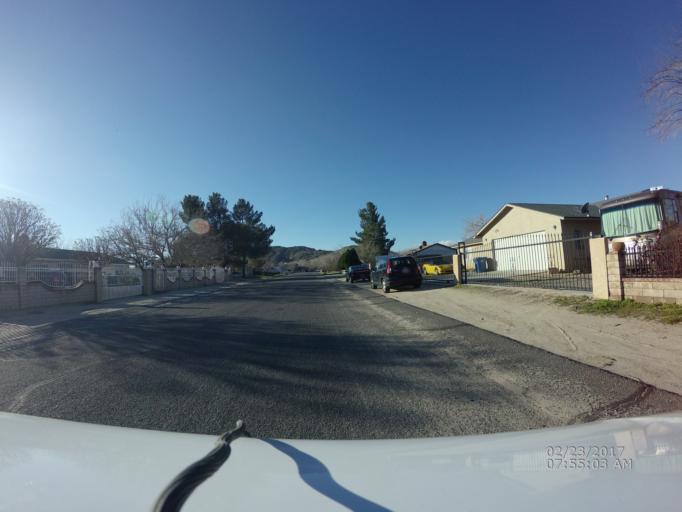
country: US
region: California
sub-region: Los Angeles County
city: Lake Los Angeles
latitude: 34.6134
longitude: -117.8171
